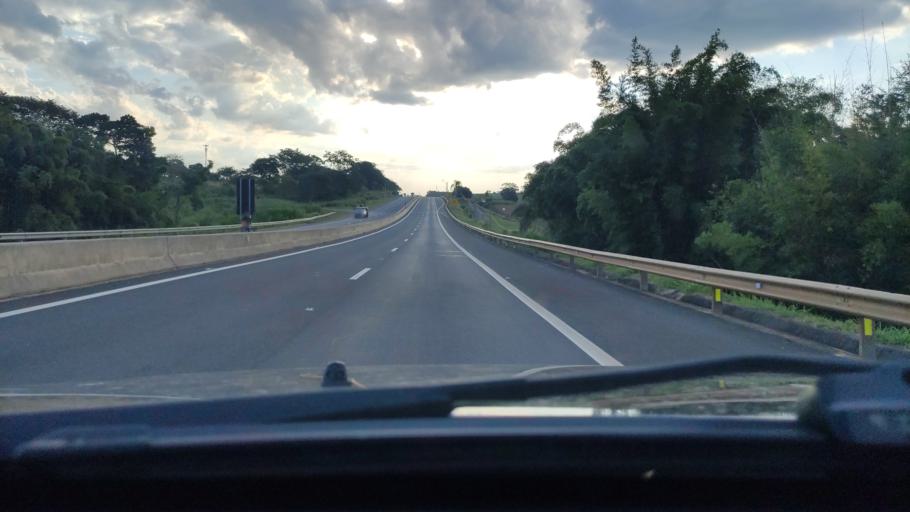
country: BR
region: Sao Paulo
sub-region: Mogi-Mirim
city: Mogi Mirim
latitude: -22.4427
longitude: -47.0406
